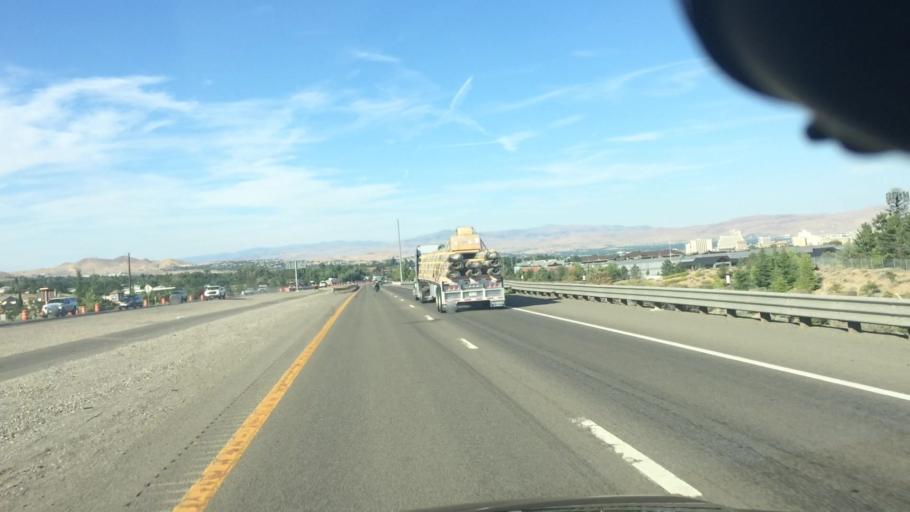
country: US
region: Nevada
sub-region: Washoe County
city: Reno
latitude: 39.5224
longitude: -119.8653
